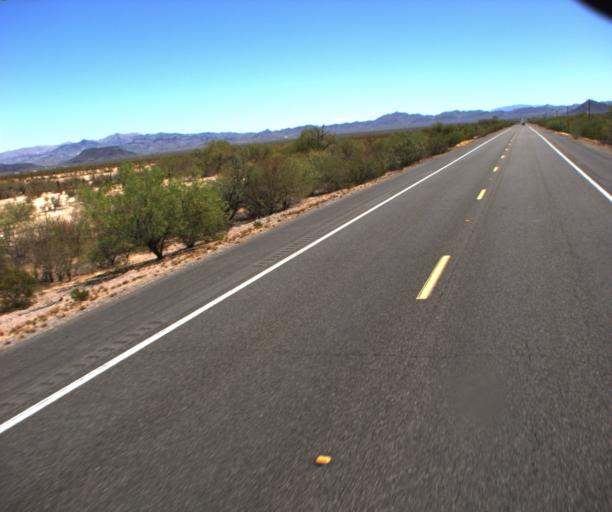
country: US
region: Arizona
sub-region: La Paz County
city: Salome
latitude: 33.7030
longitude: -113.8439
